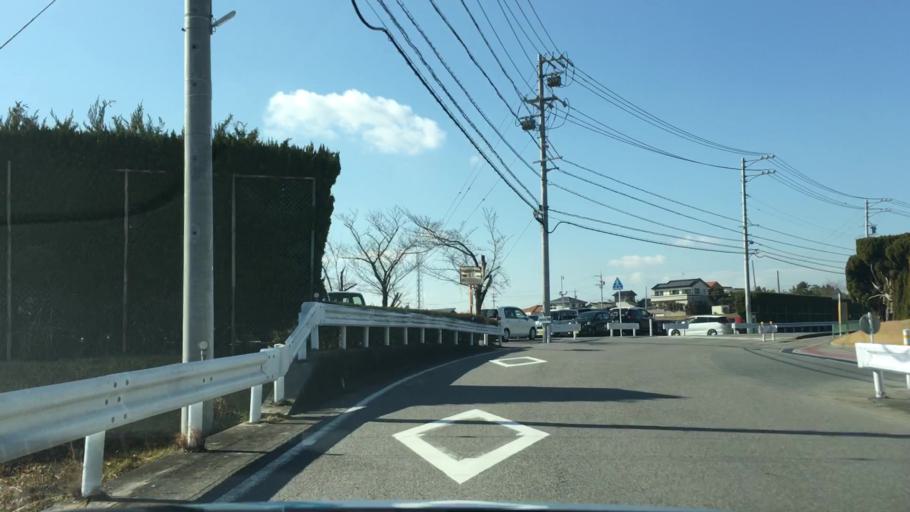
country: JP
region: Aichi
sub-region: Toyota-shi
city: Toyota
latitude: 35.0337
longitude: 137.1263
